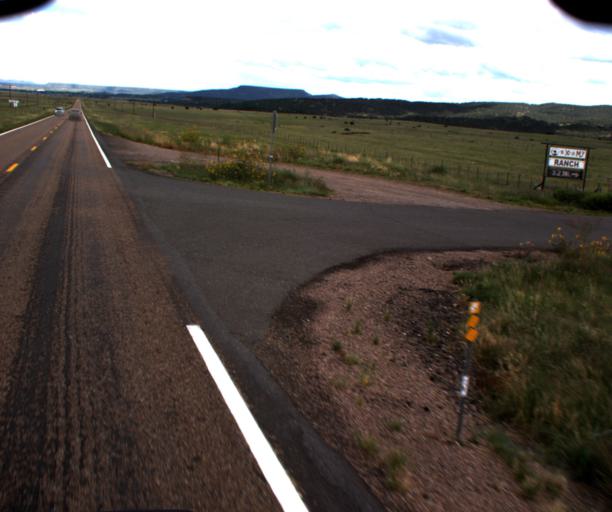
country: US
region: Arizona
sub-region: Apache County
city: Eagar
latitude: 34.1005
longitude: -109.3850
